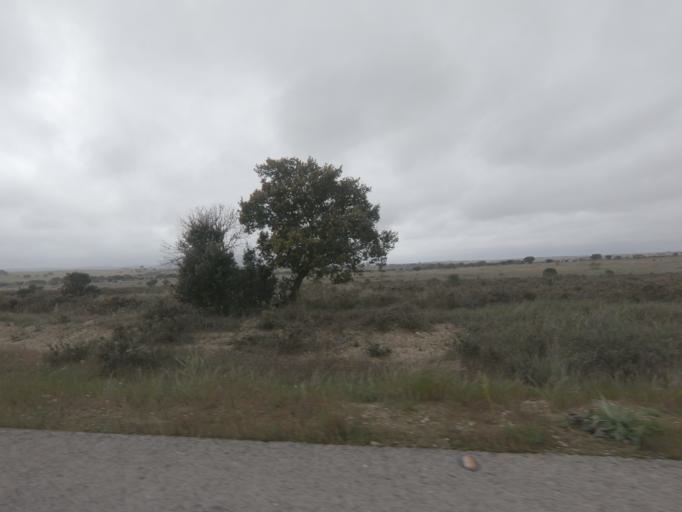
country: ES
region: Extremadura
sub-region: Provincia de Caceres
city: Malpartida de Caceres
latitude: 39.3367
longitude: -6.4815
